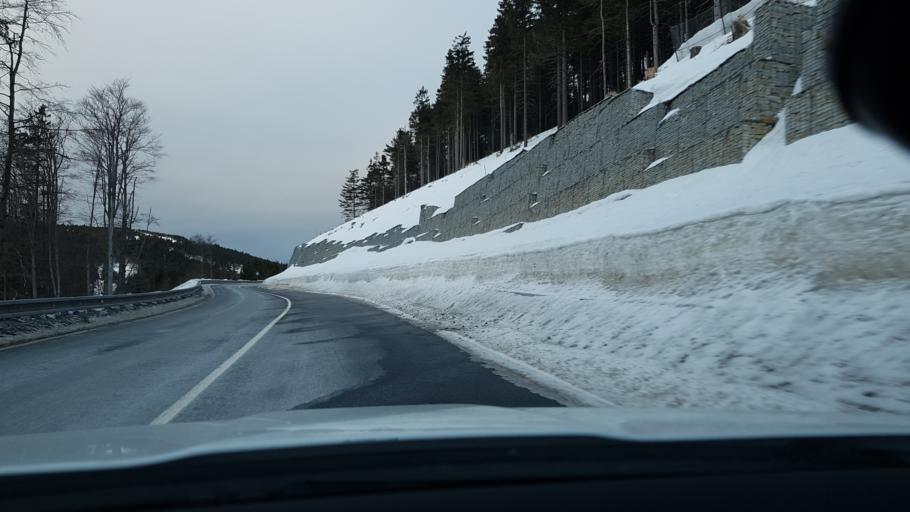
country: CZ
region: Olomoucky
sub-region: Okres Sumperk
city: Loucna nad Desnou
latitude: 50.1174
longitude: 17.1469
